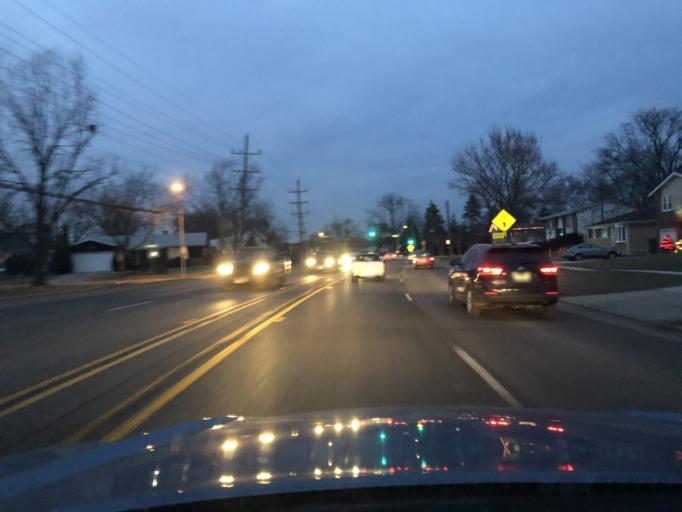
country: US
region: Illinois
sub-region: Cook County
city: Mount Prospect
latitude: 42.0430
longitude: -87.9608
